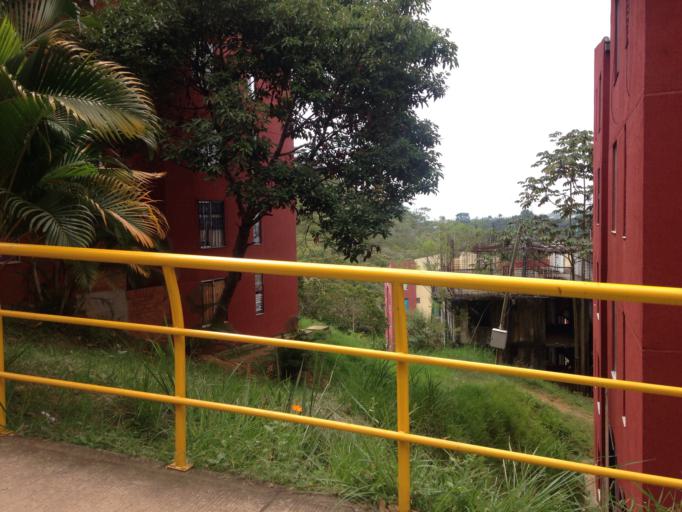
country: CO
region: Valle del Cauca
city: Cali
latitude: 3.3698
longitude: -76.5551
